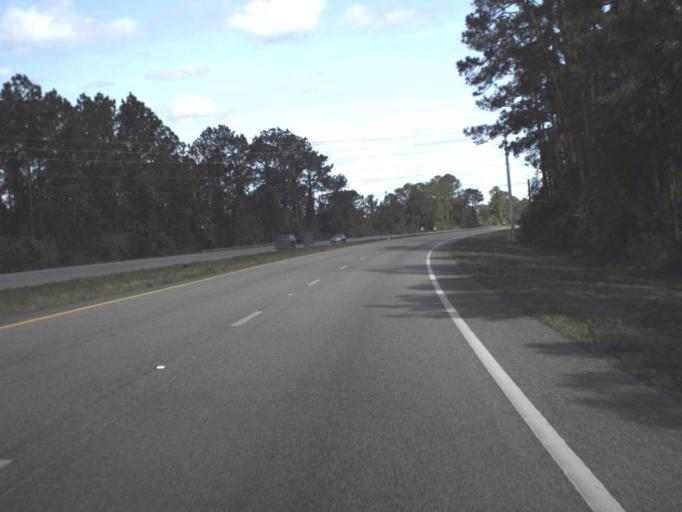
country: US
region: Florida
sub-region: Flagler County
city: Bunnell
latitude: 29.3840
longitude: -81.1877
